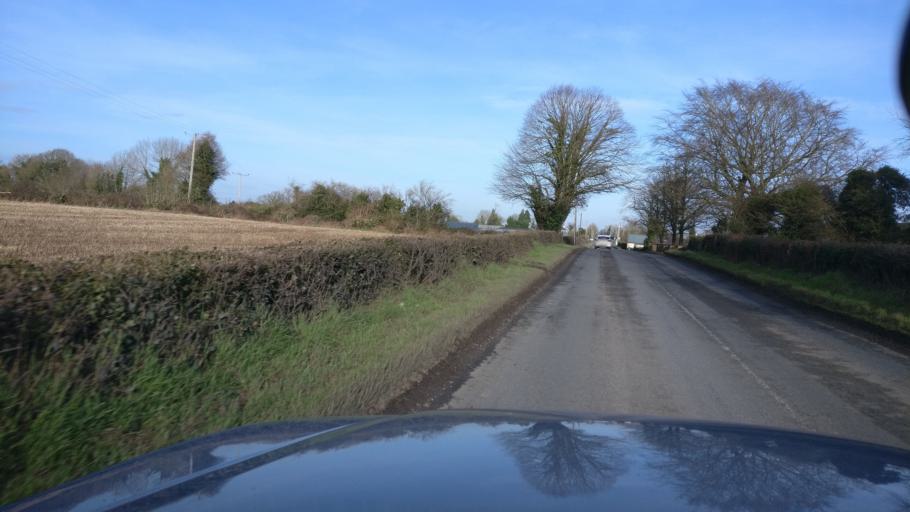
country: IE
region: Leinster
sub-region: Laois
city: Portlaoise
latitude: 53.0226
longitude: -7.2711
